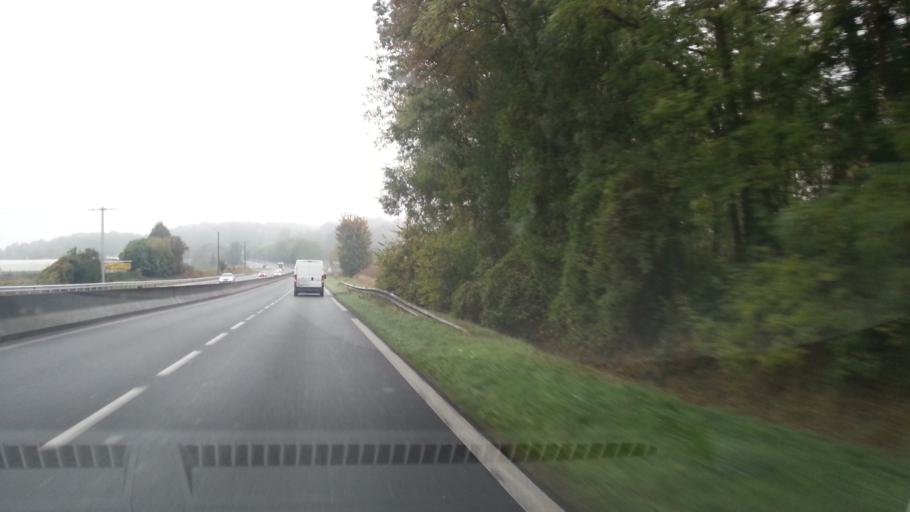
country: FR
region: Picardie
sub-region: Departement de l'Oise
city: Rantigny
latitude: 49.3353
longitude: 2.4340
